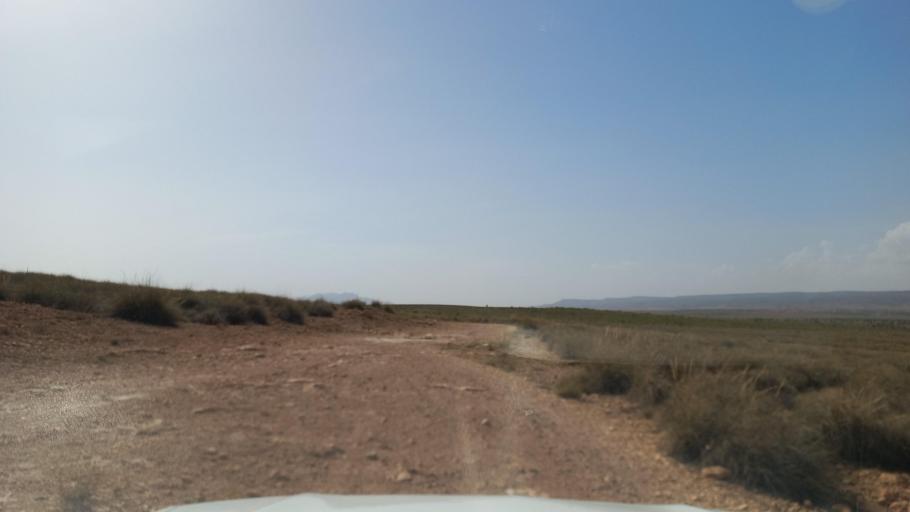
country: TN
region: Al Qasrayn
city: Kasserine
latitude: 35.2153
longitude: 8.9870
